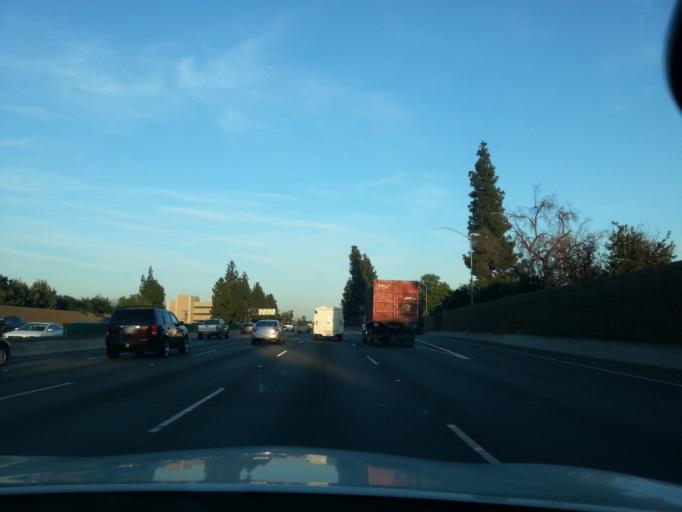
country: US
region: California
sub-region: Los Angeles County
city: Sherman Oaks
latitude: 34.1566
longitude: -118.4168
